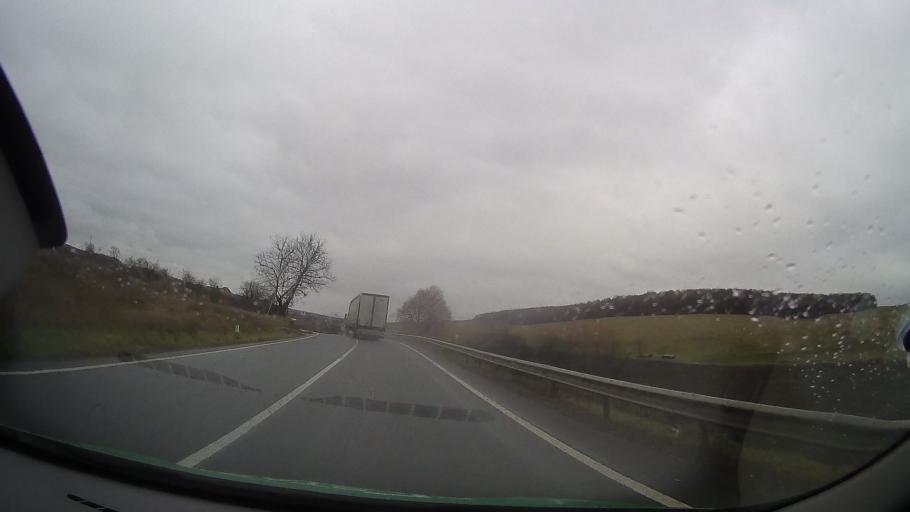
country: RO
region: Mures
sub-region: Comuna Lunca
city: Lunca
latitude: 46.8605
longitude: 24.5563
